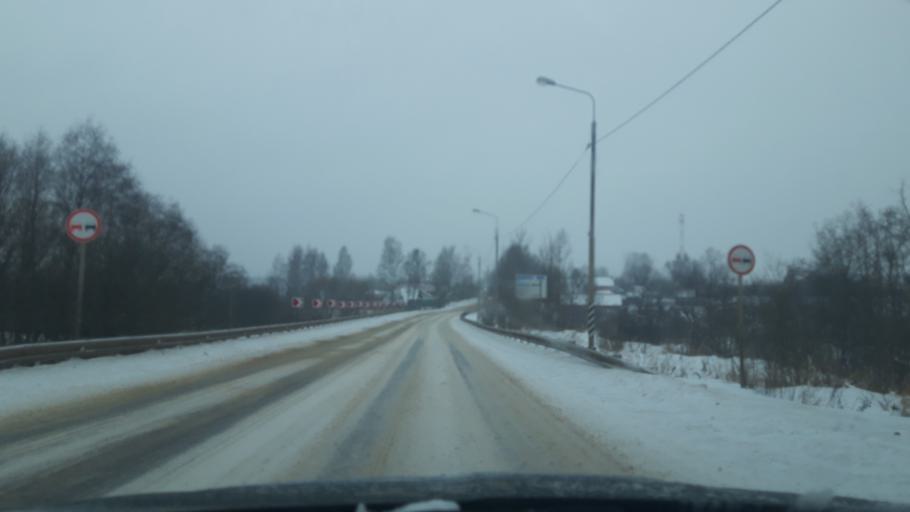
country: RU
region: Moskovskaya
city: Avtopoligon
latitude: 56.2519
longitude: 37.2322
